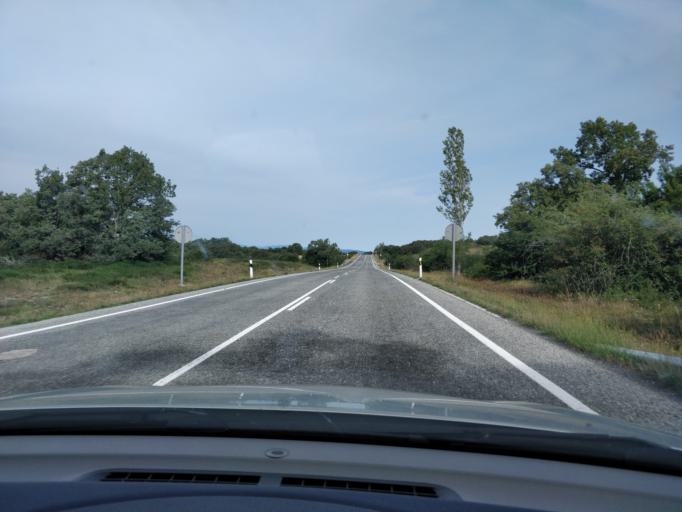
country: ES
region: Cantabria
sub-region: Provincia de Cantabria
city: San Martin de Elines
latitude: 42.9413
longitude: -3.7398
